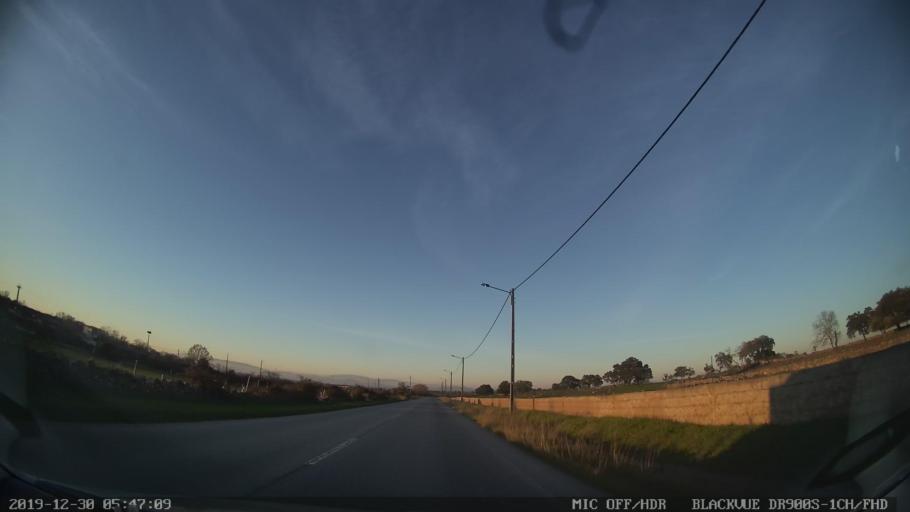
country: PT
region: Castelo Branco
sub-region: Idanha-A-Nova
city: Idanha-a-Nova
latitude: 39.9481
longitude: -7.2382
